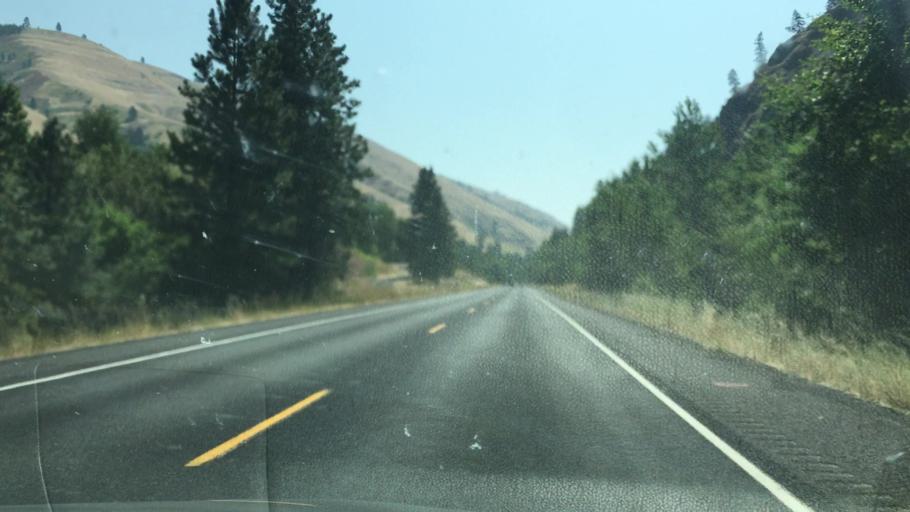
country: US
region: Idaho
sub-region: Nez Perce County
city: Lapwai
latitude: 46.3641
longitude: -116.6396
